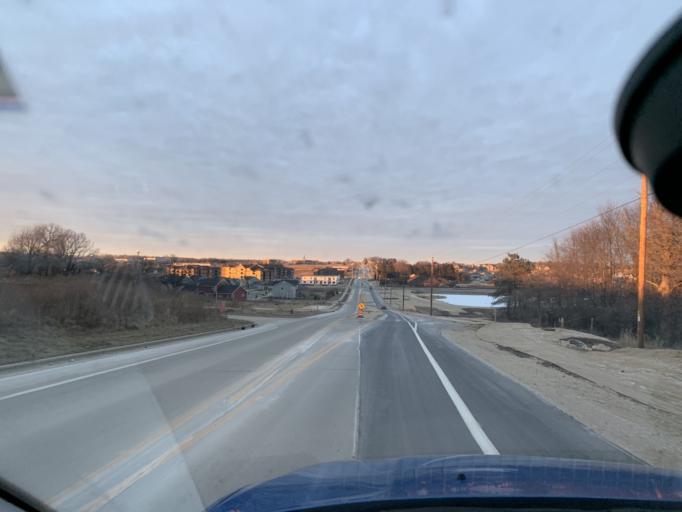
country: US
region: Wisconsin
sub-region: Dane County
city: Verona
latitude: 43.0471
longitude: -89.5523
